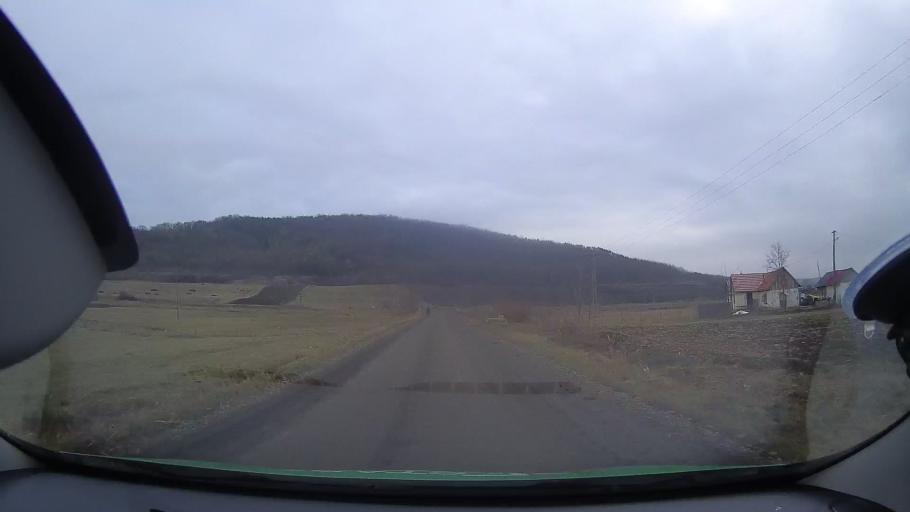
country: RO
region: Mures
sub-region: Comuna Bichis
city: Bichis
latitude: 46.3826
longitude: 24.0813
